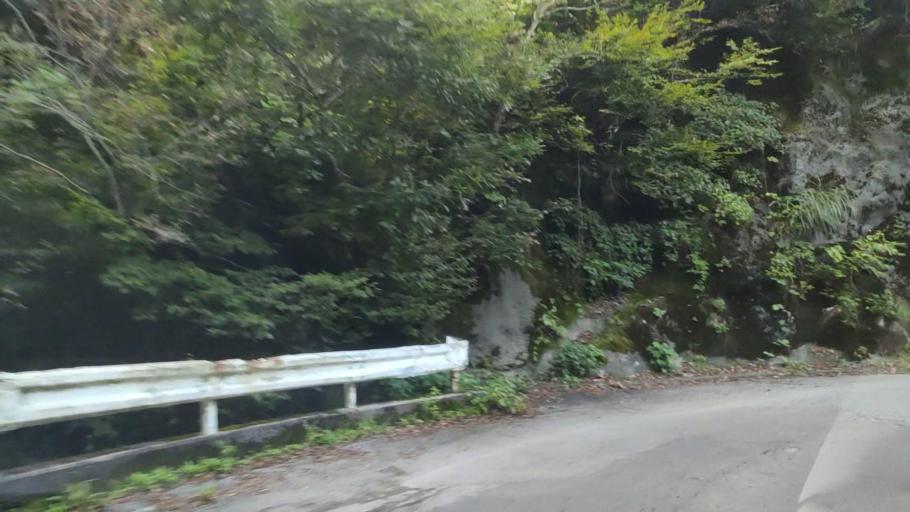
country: JP
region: Toyama
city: Yatsuomachi-higashikumisaka
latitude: 36.5020
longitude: 137.0632
